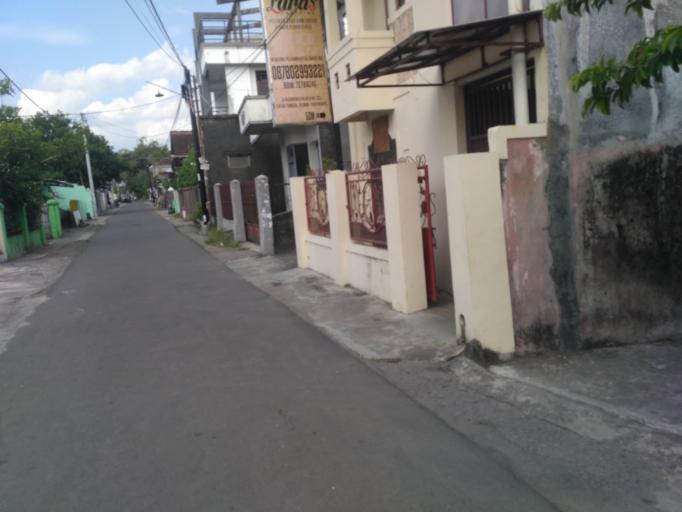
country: ID
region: Daerah Istimewa Yogyakarta
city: Depok
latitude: -7.7764
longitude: 110.4071
